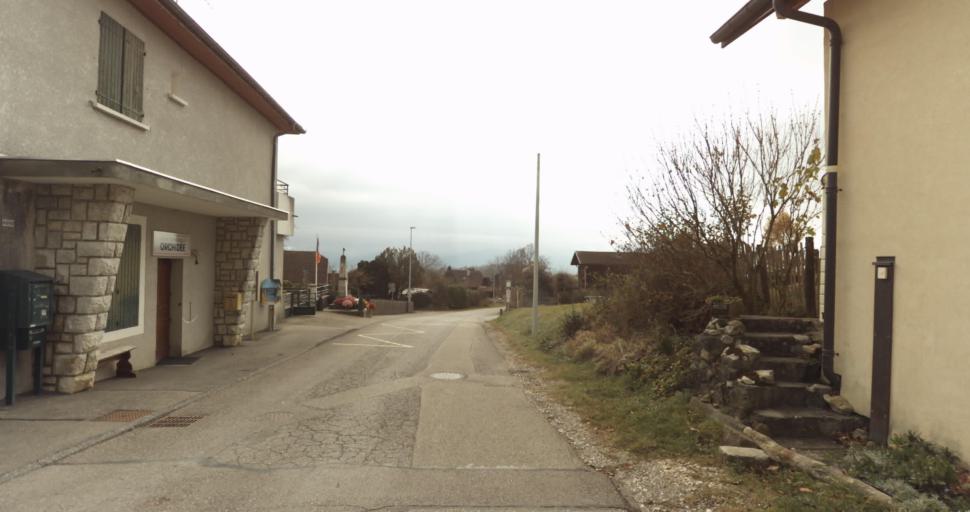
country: FR
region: Rhone-Alpes
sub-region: Departement de la Haute-Savoie
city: Epagny
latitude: 45.9673
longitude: 6.0889
